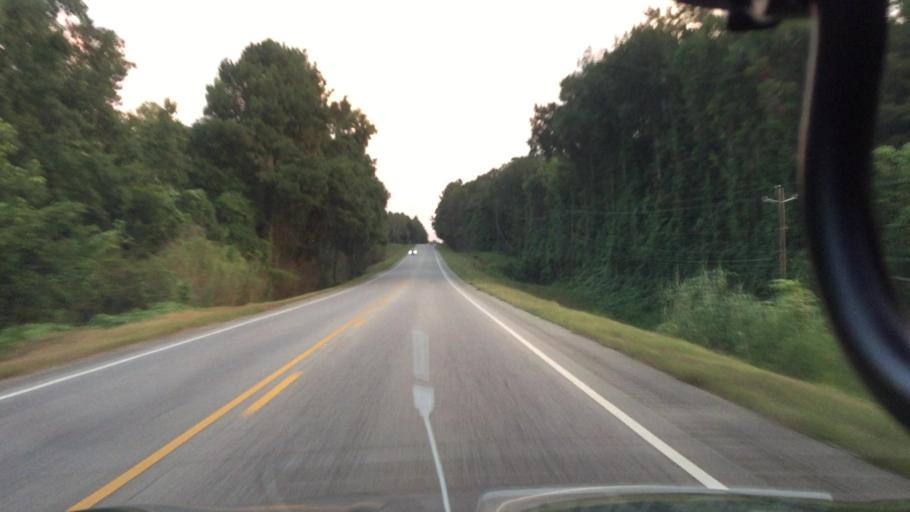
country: US
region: Alabama
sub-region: Coffee County
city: New Brockton
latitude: 31.3840
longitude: -85.8744
